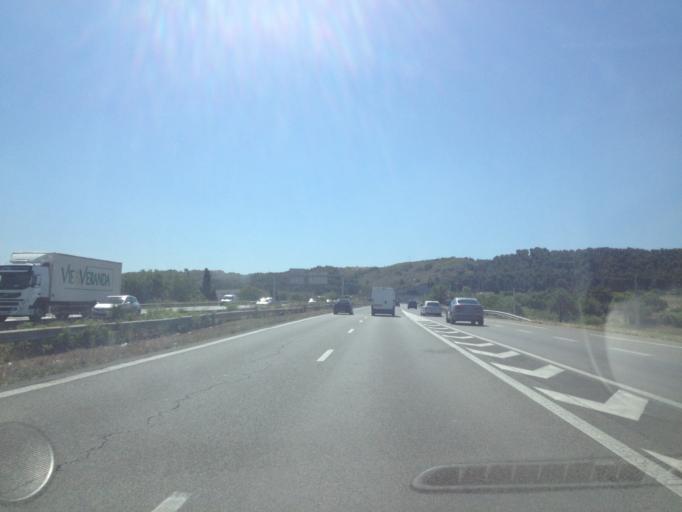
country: FR
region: Provence-Alpes-Cote d'Azur
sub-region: Departement des Bouches-du-Rhone
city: Les Pennes-Mirabeau
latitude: 43.4167
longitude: 5.2757
